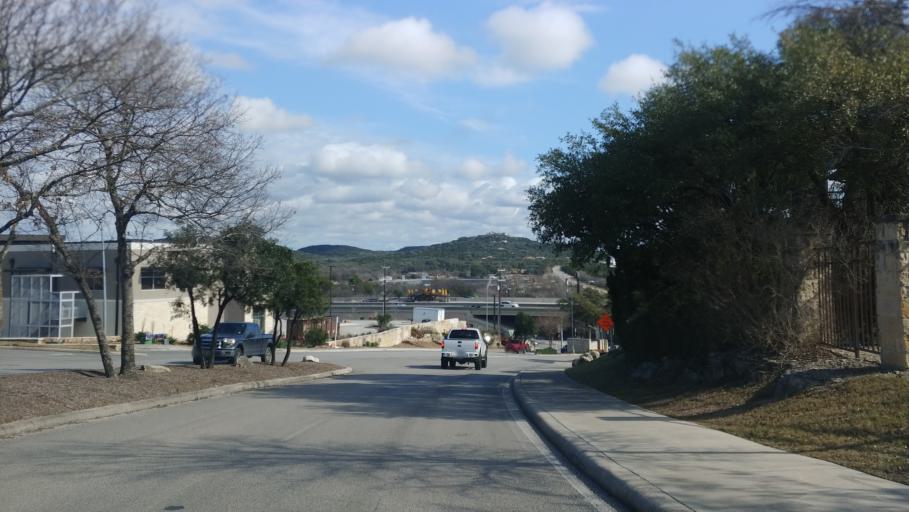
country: US
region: Texas
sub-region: Bexar County
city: Cross Mountain
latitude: 29.6243
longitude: -98.6118
